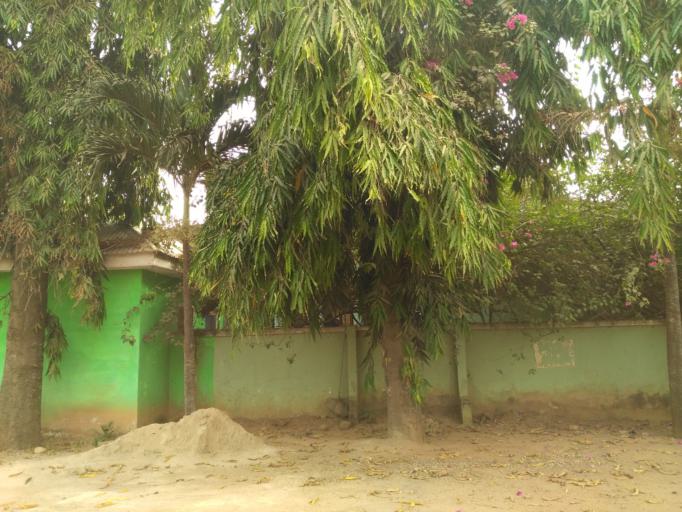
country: GH
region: Ashanti
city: Kumasi
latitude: 6.6519
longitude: -1.6243
